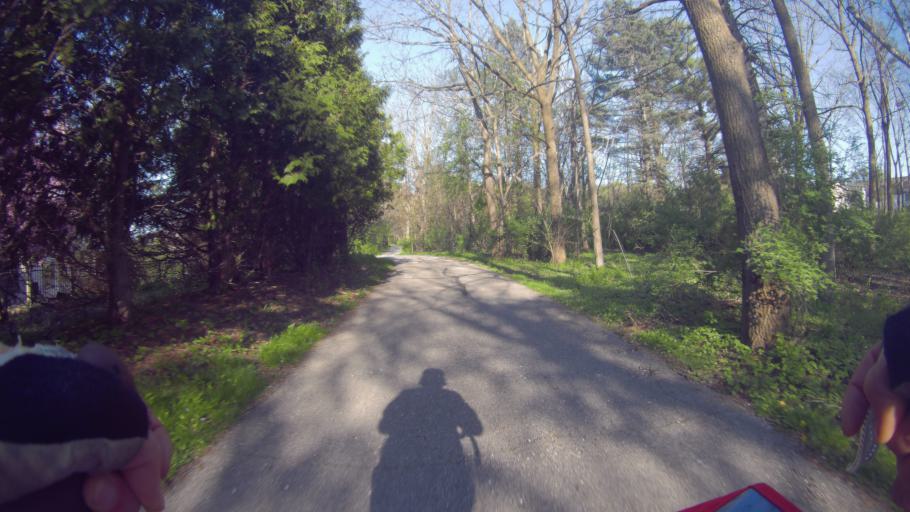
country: US
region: Wisconsin
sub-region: Dane County
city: Shorewood Hills
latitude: 43.0225
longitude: -89.4474
